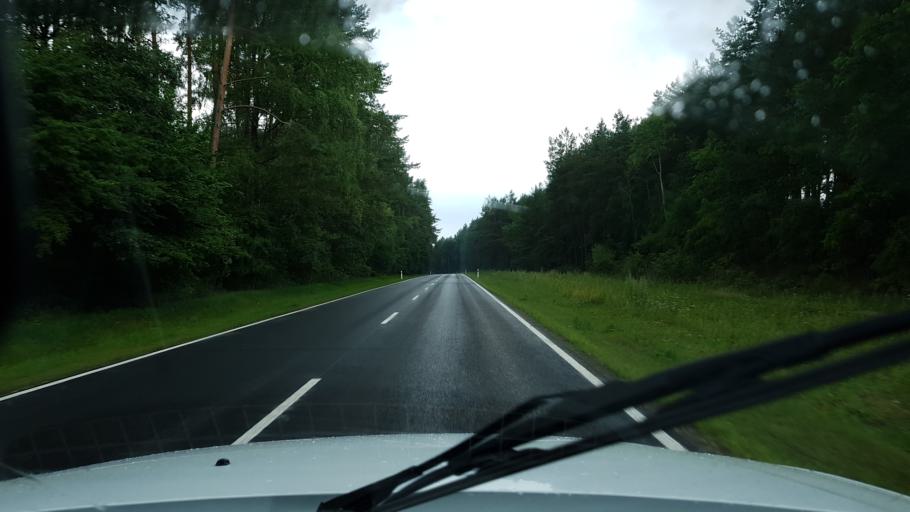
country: PL
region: West Pomeranian Voivodeship
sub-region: Powiat goleniowski
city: Mosty
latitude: 53.4396
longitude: 14.9404
